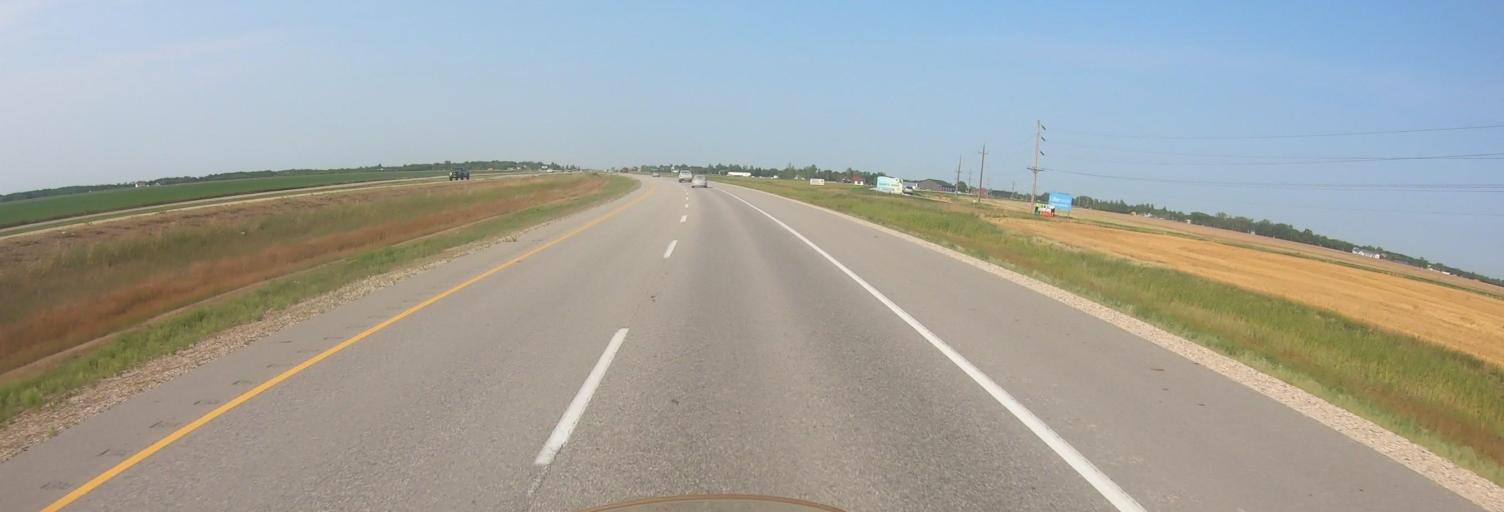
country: CA
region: Manitoba
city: Steinbach
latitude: 49.6576
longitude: -96.6697
